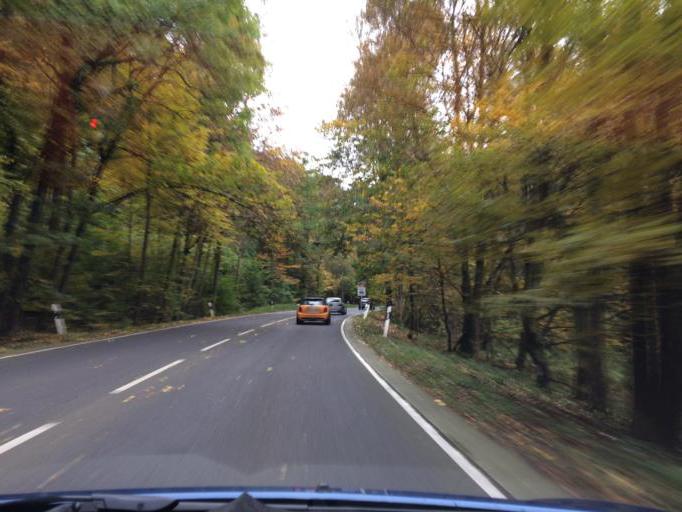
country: DE
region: North Rhine-Westphalia
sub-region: Regierungsbezirk Koln
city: Konigswinter
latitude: 50.6800
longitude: 7.2224
